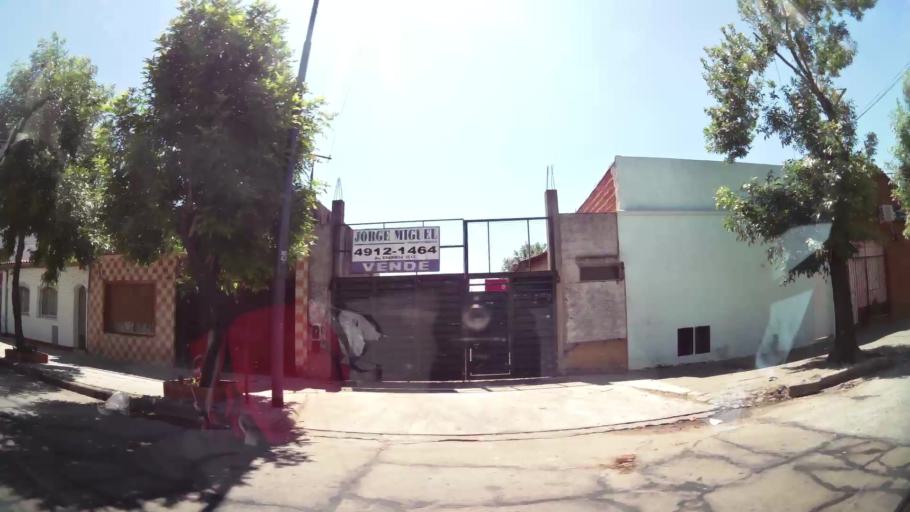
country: AR
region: Buenos Aires
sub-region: Partido de Avellaneda
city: Avellaneda
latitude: -34.6573
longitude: -58.4090
